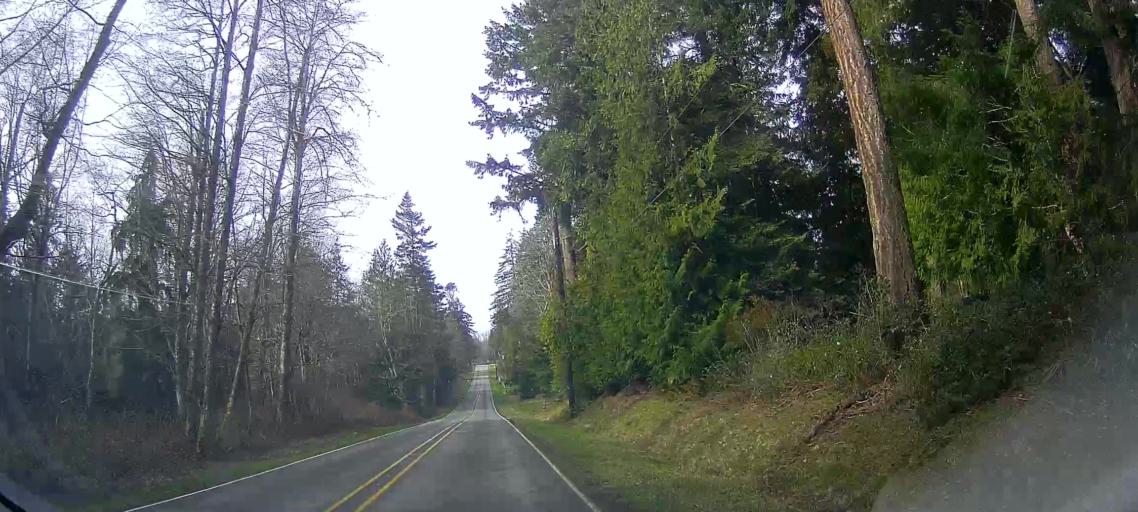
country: US
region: Washington
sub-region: Island County
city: Langley
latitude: 48.0871
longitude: -122.3856
